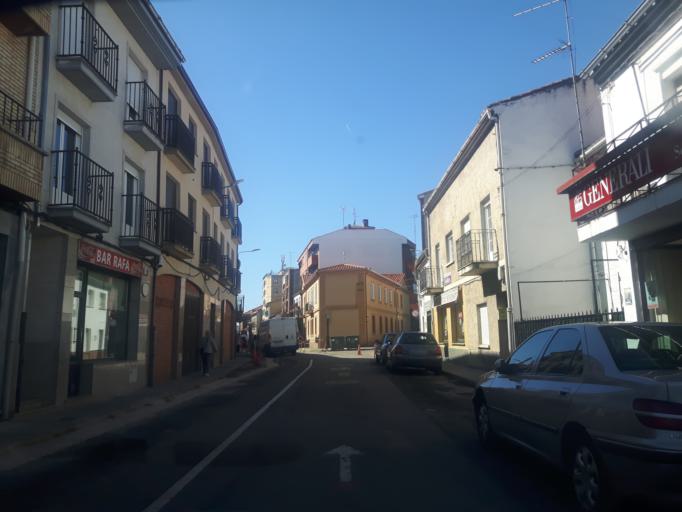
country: ES
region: Castille and Leon
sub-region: Provincia de Salamanca
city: Vitigudino
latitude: 41.0107
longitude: -6.4346
